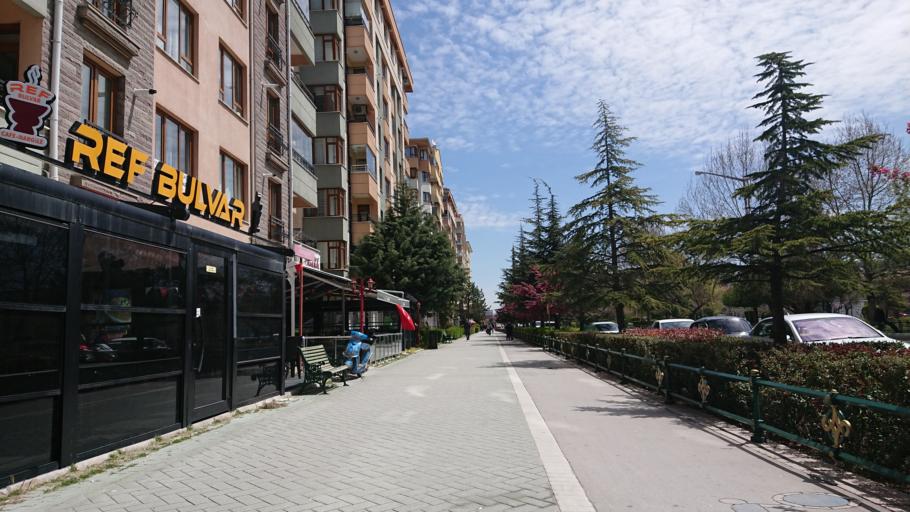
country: TR
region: Eskisehir
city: Eskisehir
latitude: 39.7652
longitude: 30.5062
